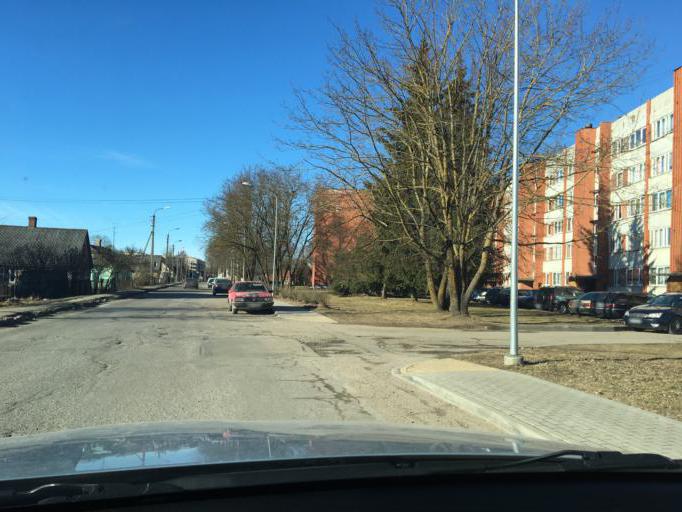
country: LV
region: Jekabpils Rajons
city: Jekabpils
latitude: 56.4884
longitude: 25.8658
